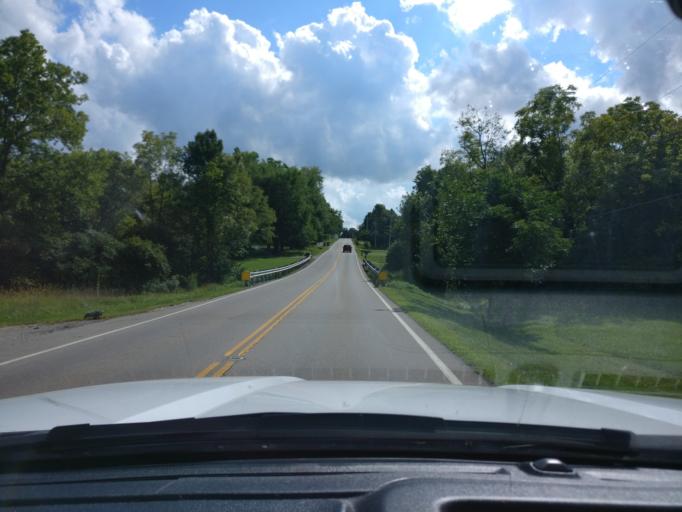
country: US
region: Ohio
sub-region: Warren County
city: Five Points
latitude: 39.5339
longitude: -84.1730
